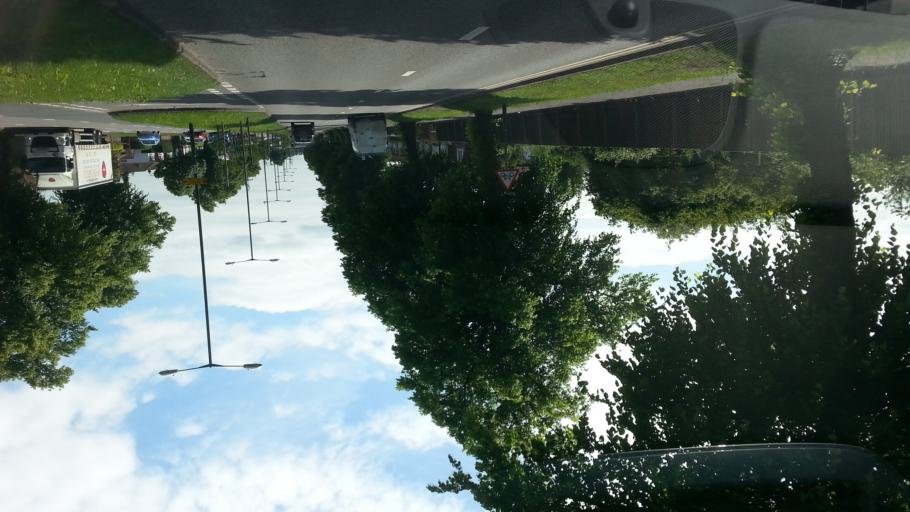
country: GB
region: England
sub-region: Nottingham
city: Nottingham
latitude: 52.9645
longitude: -1.1908
